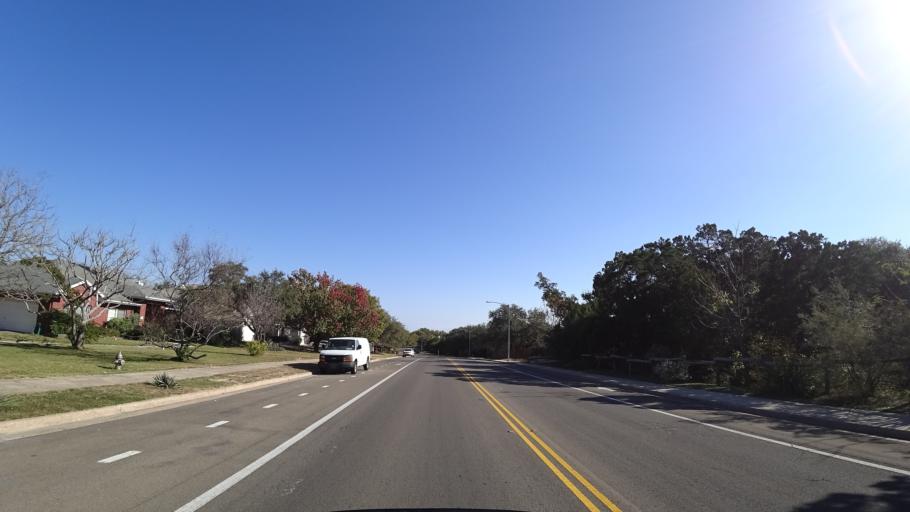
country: US
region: Texas
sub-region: Travis County
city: Barton Creek
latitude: 30.2274
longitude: -97.8721
